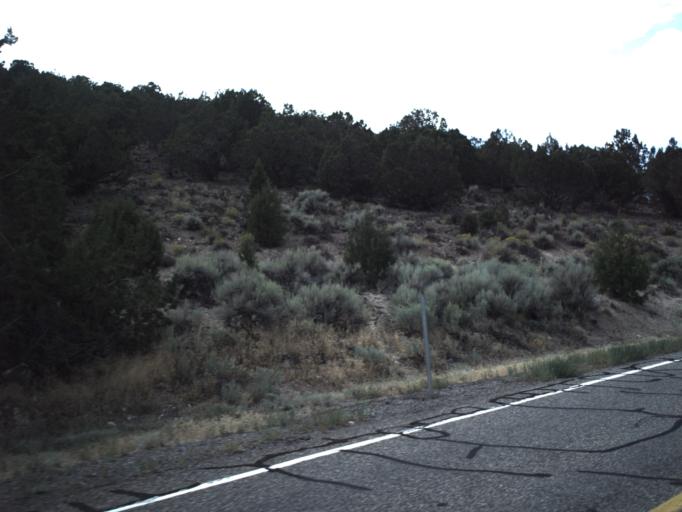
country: US
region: Utah
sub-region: Sevier County
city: Aurora
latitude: 38.7763
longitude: -111.9345
